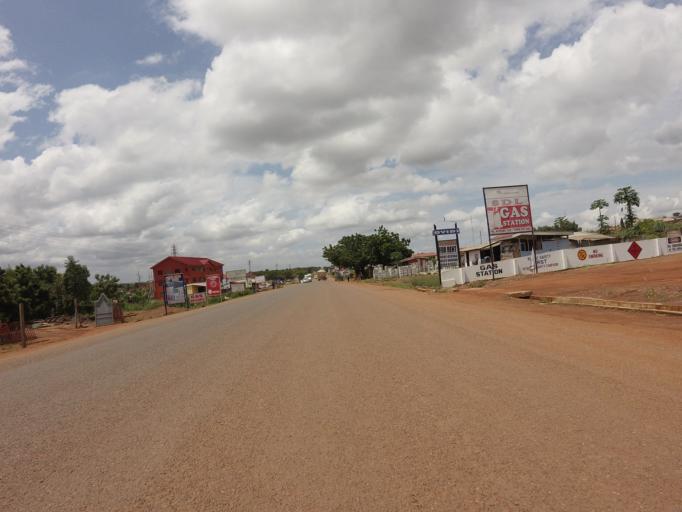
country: GH
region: Eastern
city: Aburi
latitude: 5.8123
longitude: -0.1227
